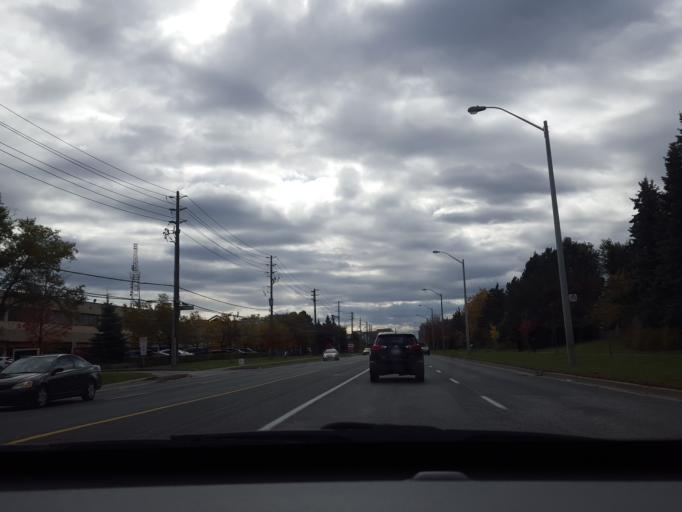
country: CA
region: Ontario
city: Markham
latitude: 43.8227
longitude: -79.3066
